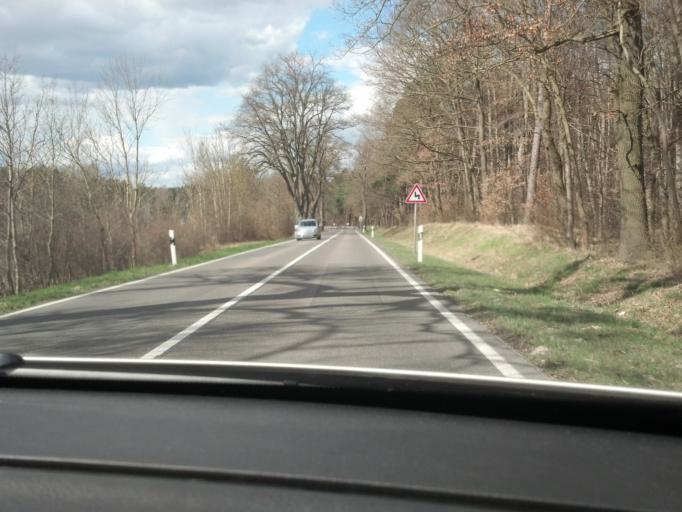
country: DE
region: Mecklenburg-Vorpommern
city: Burg Stargard
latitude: 53.4804
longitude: 13.3381
